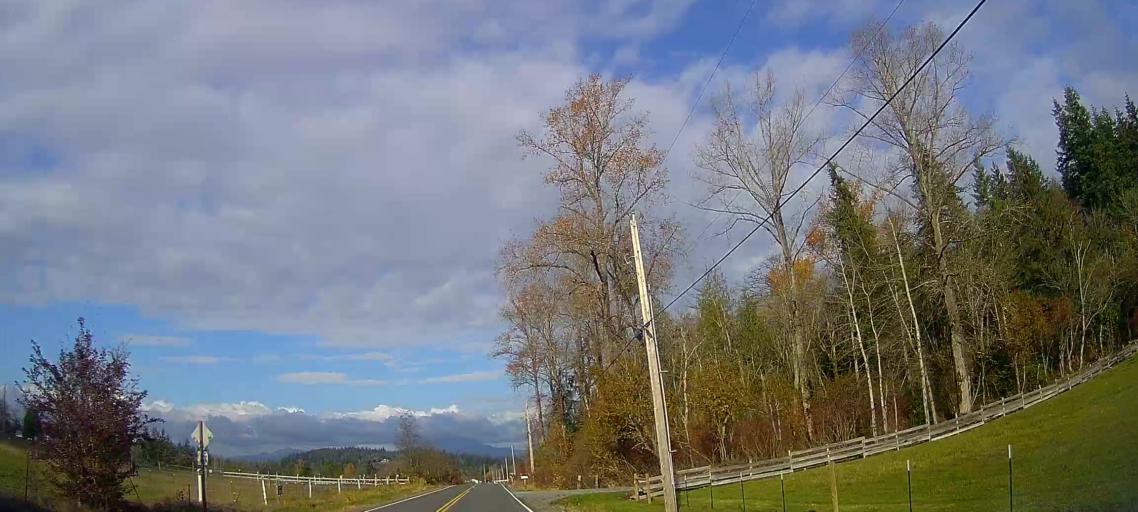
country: US
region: Washington
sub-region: Skagit County
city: Big Lake
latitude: 48.4293
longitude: -122.2425
